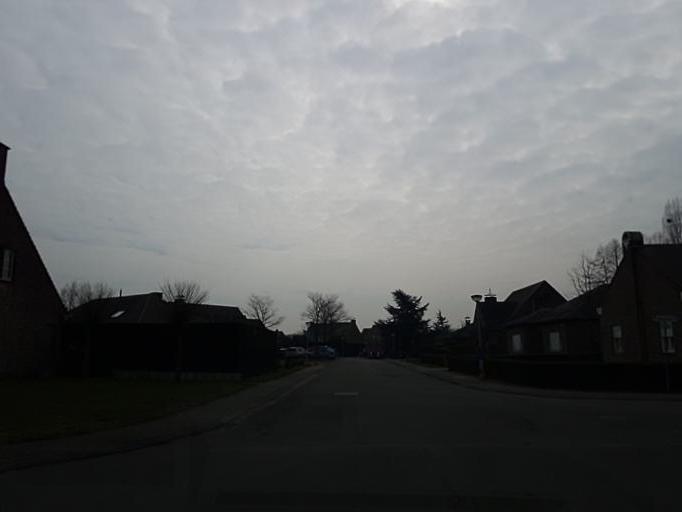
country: BE
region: Flanders
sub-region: Provincie Oost-Vlaanderen
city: Sint-Gillis-Waas
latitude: 51.2925
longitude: 4.1771
